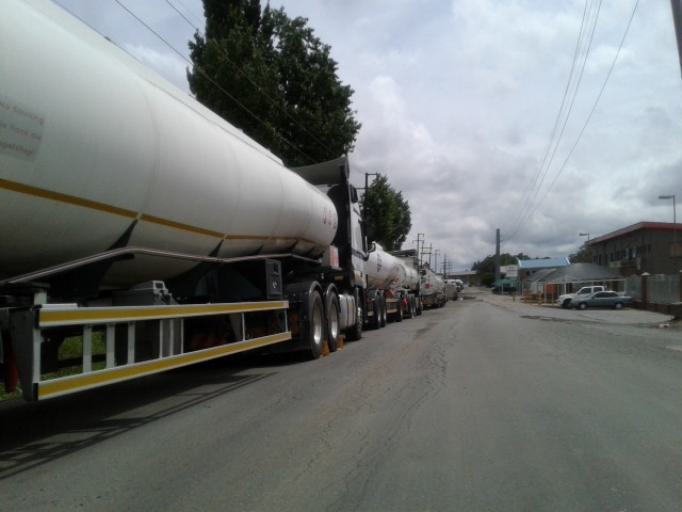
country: LS
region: Maseru
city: Maseru
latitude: -29.2976
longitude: 27.4760
